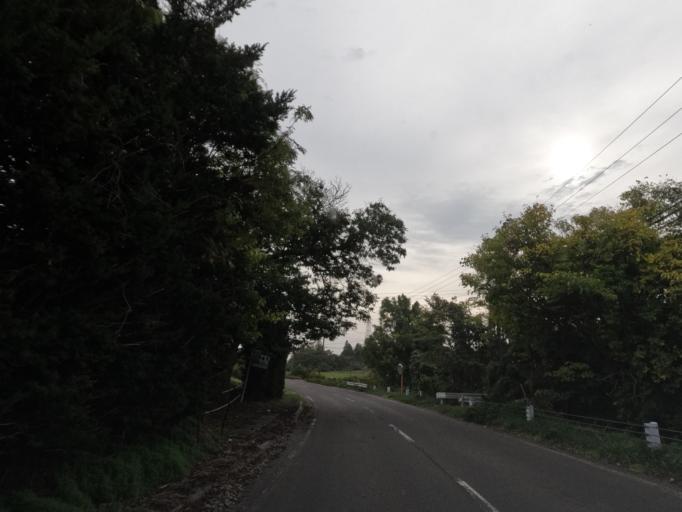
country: JP
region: Hokkaido
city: Date
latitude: 42.4617
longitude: 140.9042
